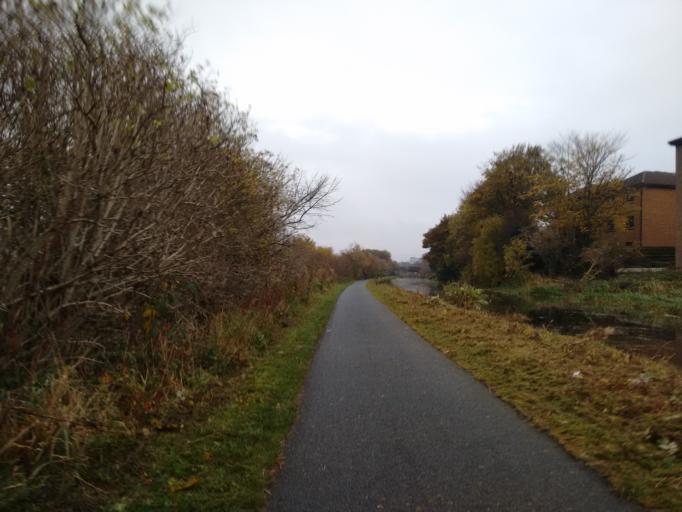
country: GB
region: Scotland
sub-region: Edinburgh
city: Colinton
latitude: 55.9261
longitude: -3.2354
